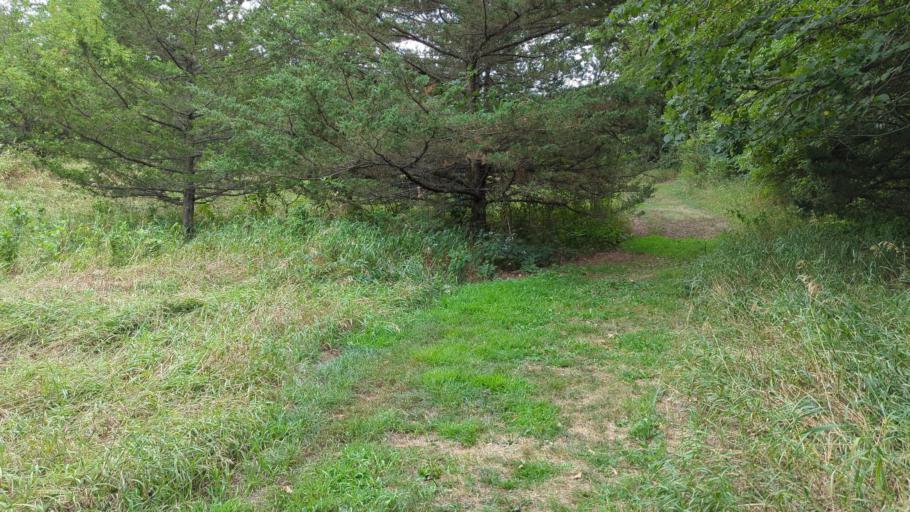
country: US
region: South Dakota
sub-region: Union County
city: Beresford
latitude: 42.9243
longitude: -96.7793
